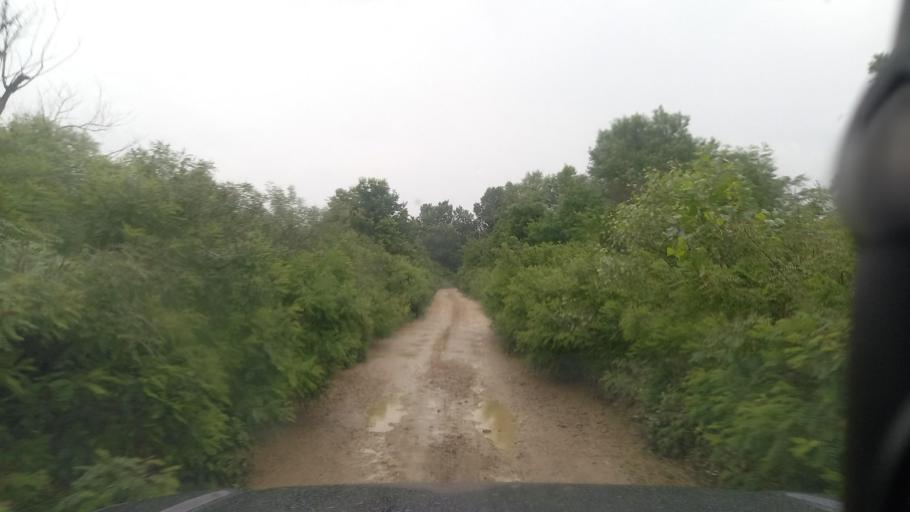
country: RU
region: Krasnodarskiy
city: Vasyurinskaya
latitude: 45.0299
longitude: 39.4753
